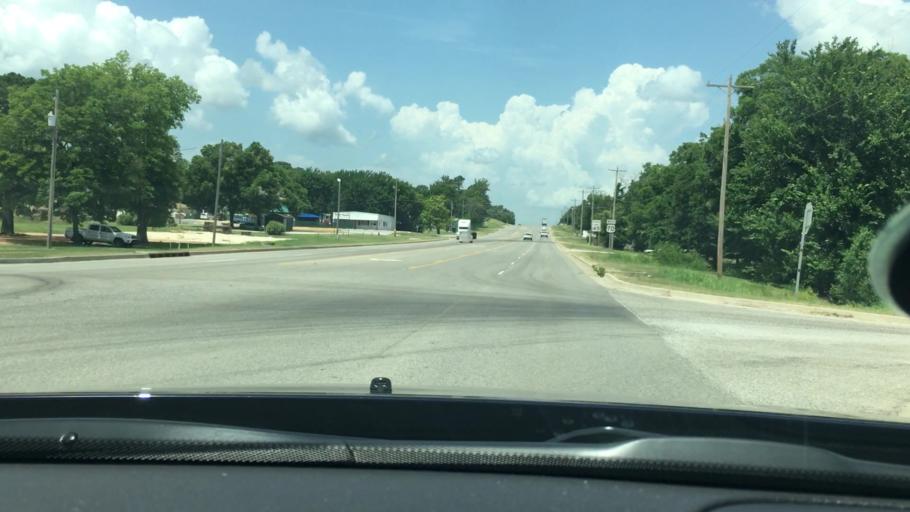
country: US
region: Oklahoma
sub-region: Marshall County
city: Oakland
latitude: 34.1000
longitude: -96.7921
